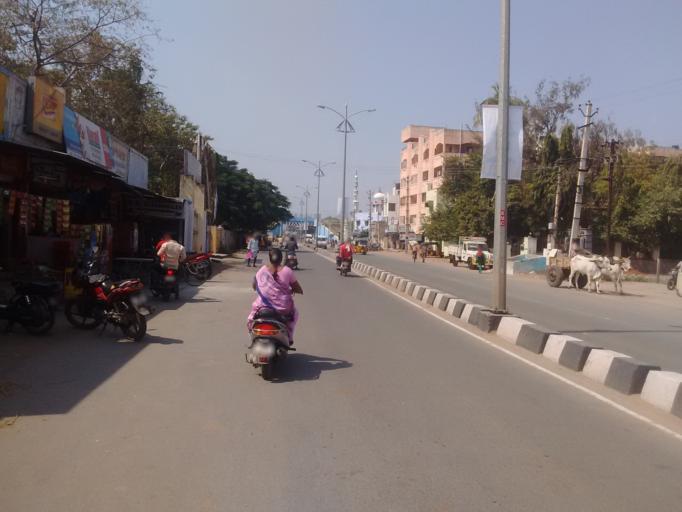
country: IN
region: Telangana
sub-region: Mahbubnagar
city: Alampur
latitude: 15.8401
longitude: 78.0367
